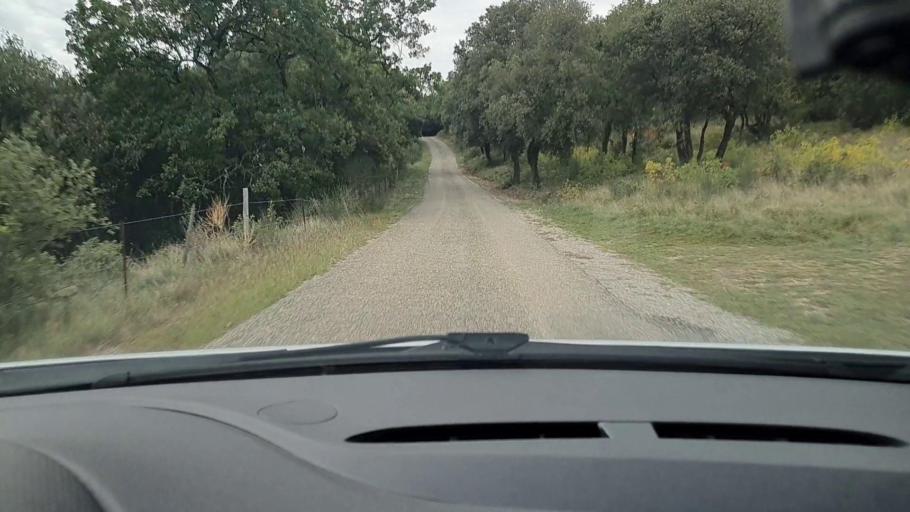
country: FR
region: Languedoc-Roussillon
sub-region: Departement du Gard
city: Mons
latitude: 44.1442
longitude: 4.2910
